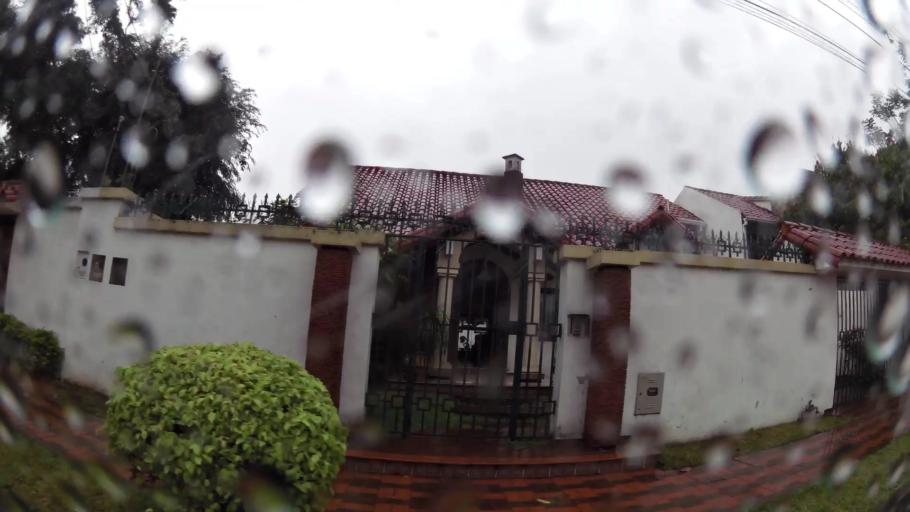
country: BO
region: Santa Cruz
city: Santa Cruz de la Sierra
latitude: -17.8019
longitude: -63.1631
